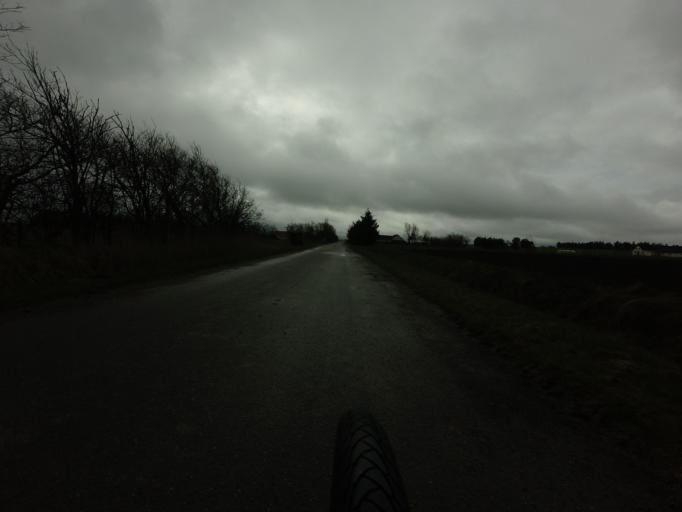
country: DK
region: North Denmark
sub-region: Hjorring Kommune
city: Vra
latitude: 57.3810
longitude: 9.8386
